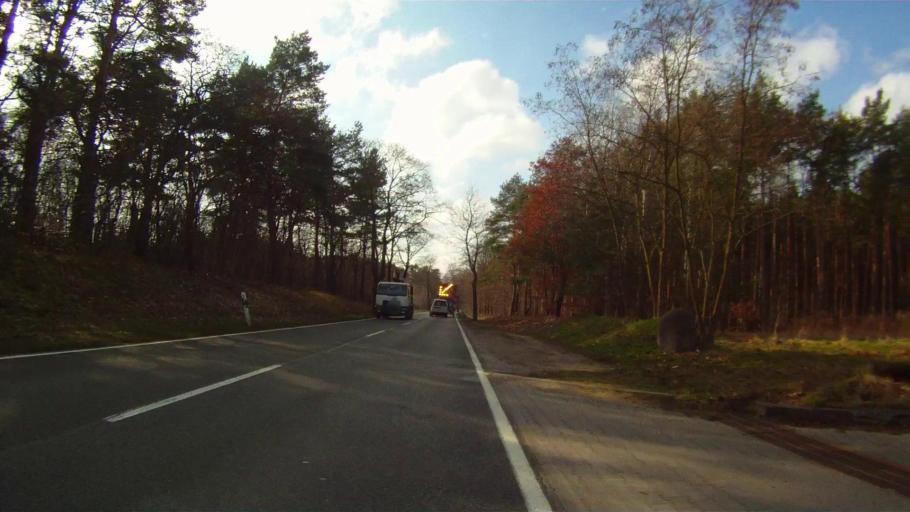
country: DE
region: Brandenburg
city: Erkner
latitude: 52.3817
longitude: 13.7222
